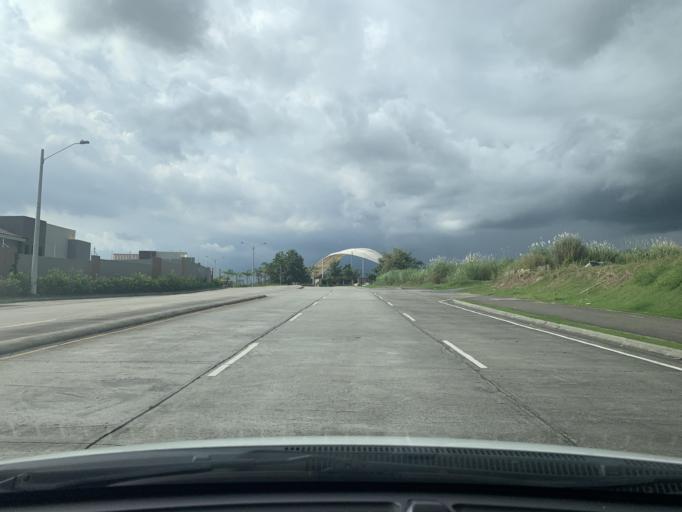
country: PA
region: Panama
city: San Miguelito
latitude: 9.0906
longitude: -79.4679
